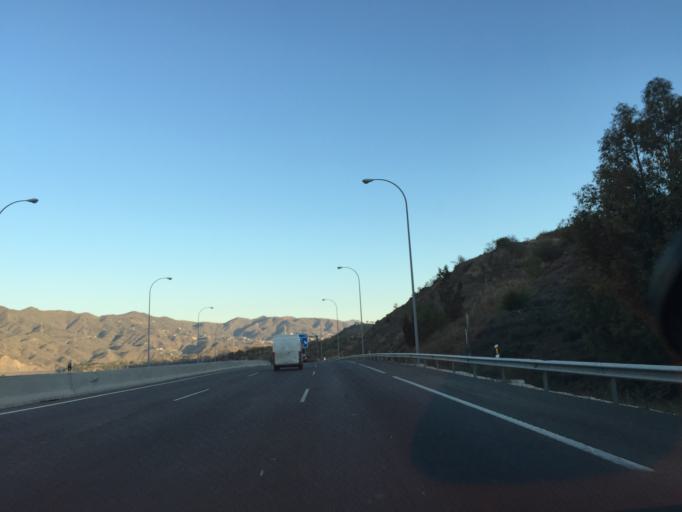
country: ES
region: Andalusia
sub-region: Provincia de Malaga
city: Malaga
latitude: 36.7463
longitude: -4.4083
